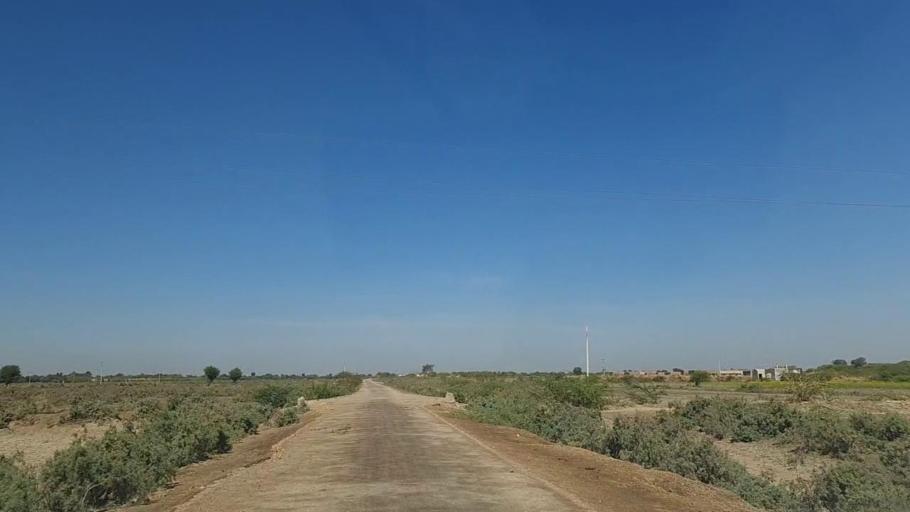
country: PK
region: Sindh
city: Samaro
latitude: 25.3023
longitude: 69.4858
